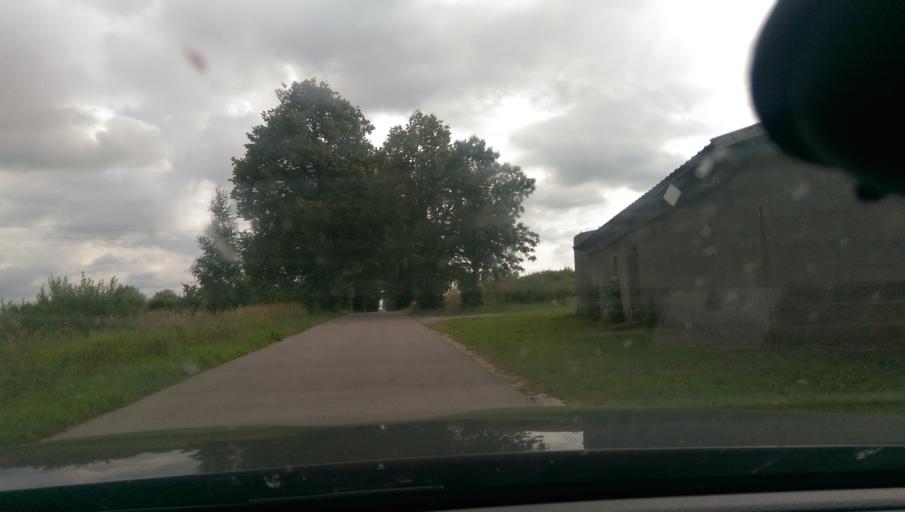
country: PL
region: Warmian-Masurian Voivodeship
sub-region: Powiat wegorzewski
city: Pozezdrze
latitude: 54.1918
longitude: 21.9180
